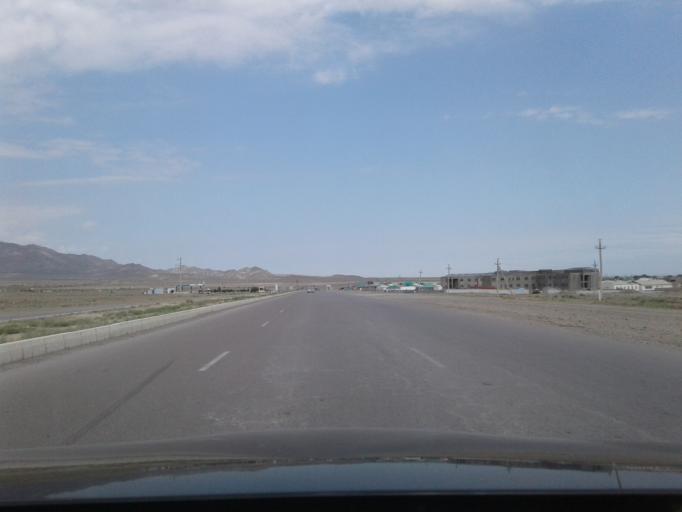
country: TM
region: Ahal
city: Baharly
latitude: 38.5353
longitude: 57.1600
